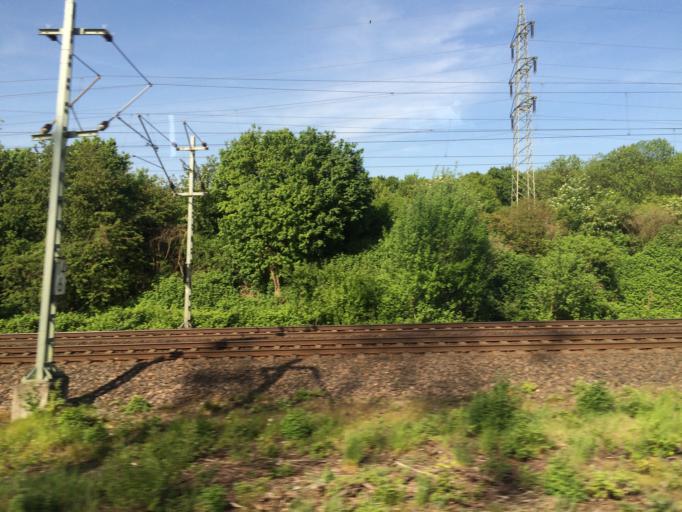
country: DE
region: North Rhine-Westphalia
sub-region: Regierungsbezirk Koln
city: Leverkusen
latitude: 51.0561
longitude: 6.9790
